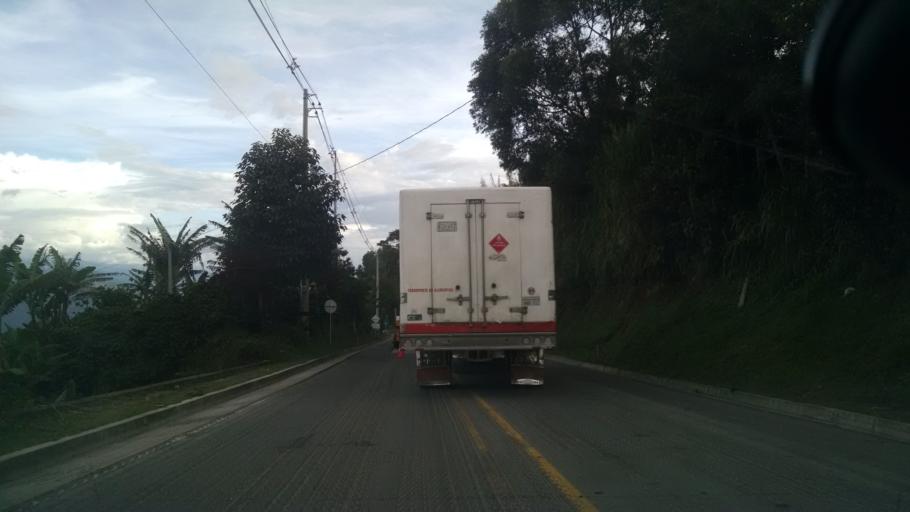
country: CO
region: Antioquia
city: Santa Barbara
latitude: 5.8970
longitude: -75.5722
